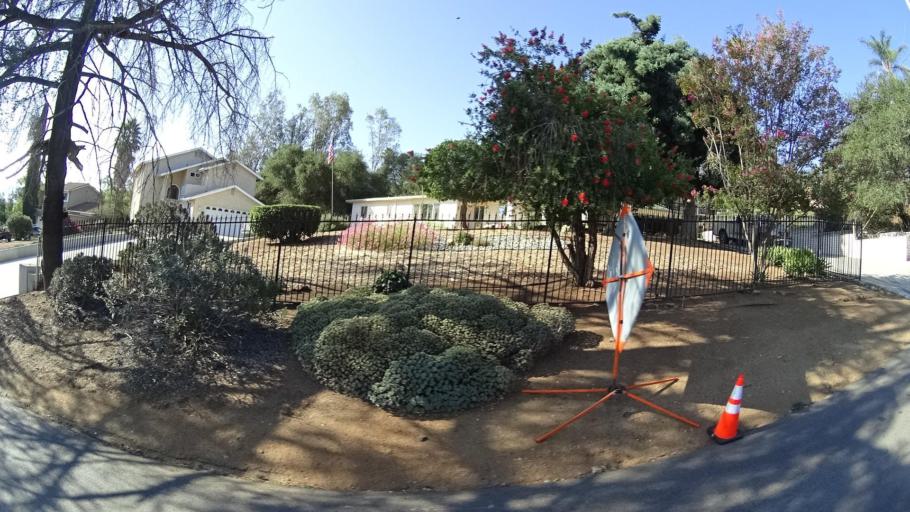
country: US
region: California
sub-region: San Diego County
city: Escondido
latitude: 33.0910
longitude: -117.0745
